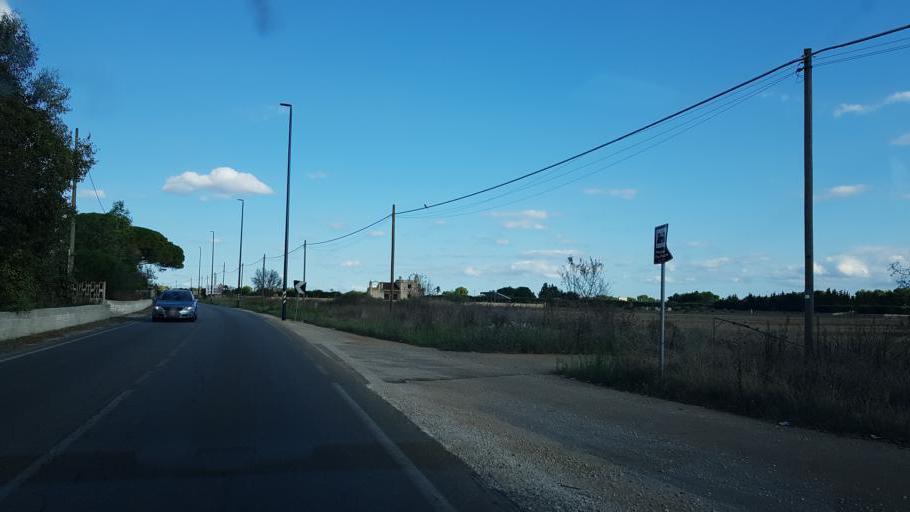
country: IT
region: Apulia
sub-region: Provincia di Lecce
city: Nardo
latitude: 40.1279
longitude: 18.0224
